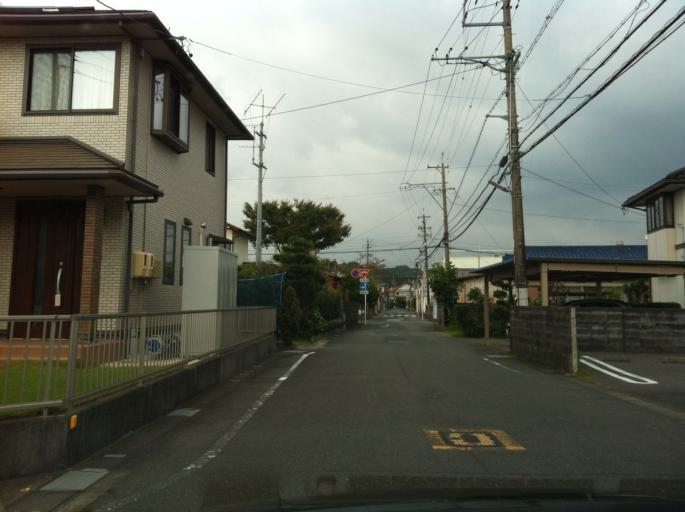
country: JP
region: Shizuoka
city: Kakegawa
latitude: 34.7772
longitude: 138.0072
